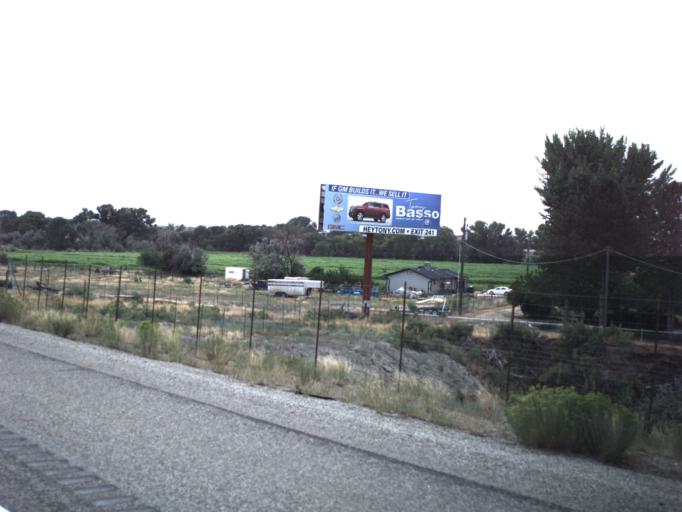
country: US
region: Utah
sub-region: Carbon County
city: Carbonville
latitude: 39.6169
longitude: -110.8523
